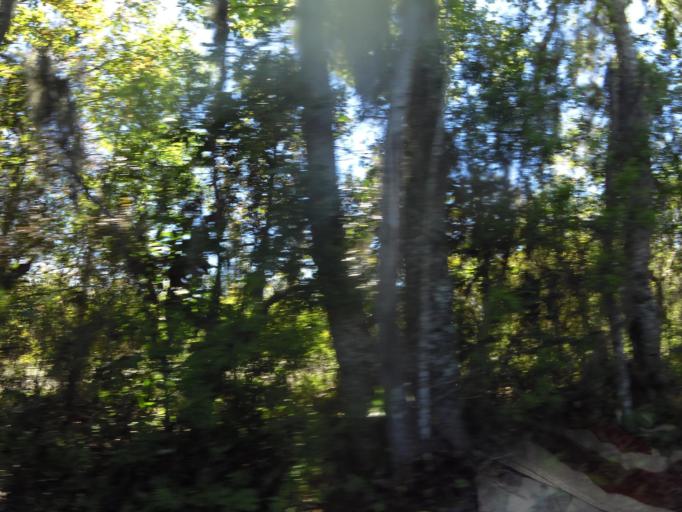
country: US
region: Florida
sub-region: Bradford County
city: Starke
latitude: 30.0467
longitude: -82.0558
